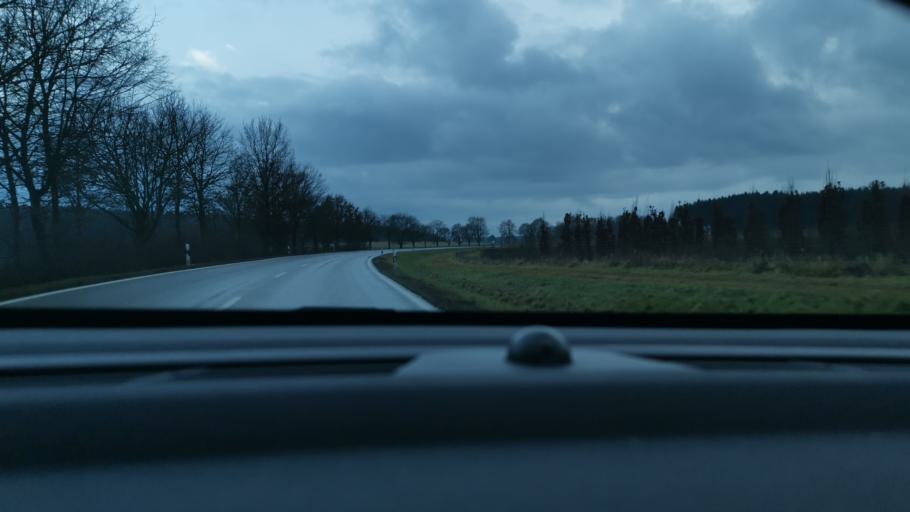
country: DE
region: Bavaria
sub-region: Swabia
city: Petersdorf
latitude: 48.5012
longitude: 11.0166
